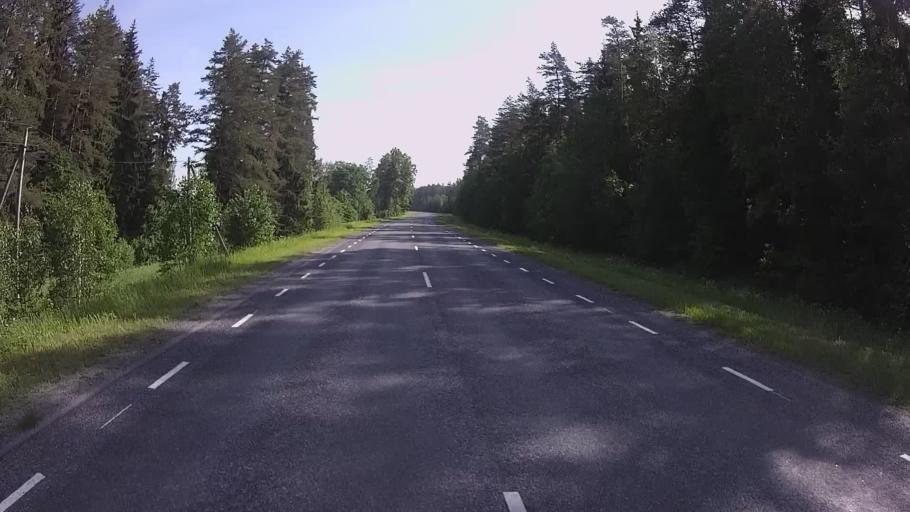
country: EE
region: Valgamaa
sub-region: Torva linn
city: Torva
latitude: 58.0248
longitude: 25.9579
